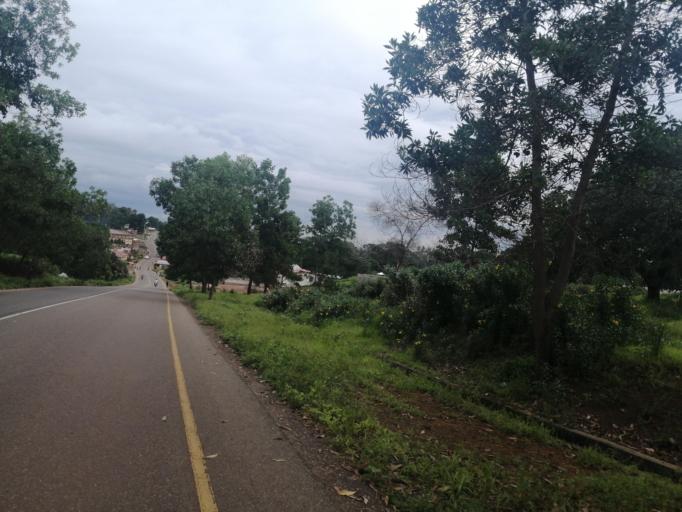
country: SL
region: Northern Province
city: Port Loko
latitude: 8.7728
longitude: -12.7856
